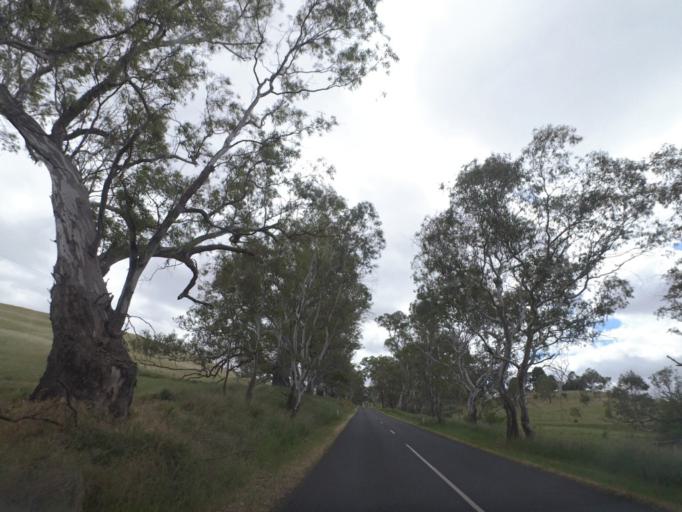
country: AU
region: Victoria
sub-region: Whittlesea
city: Whittlesea
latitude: -37.1933
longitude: 145.0384
